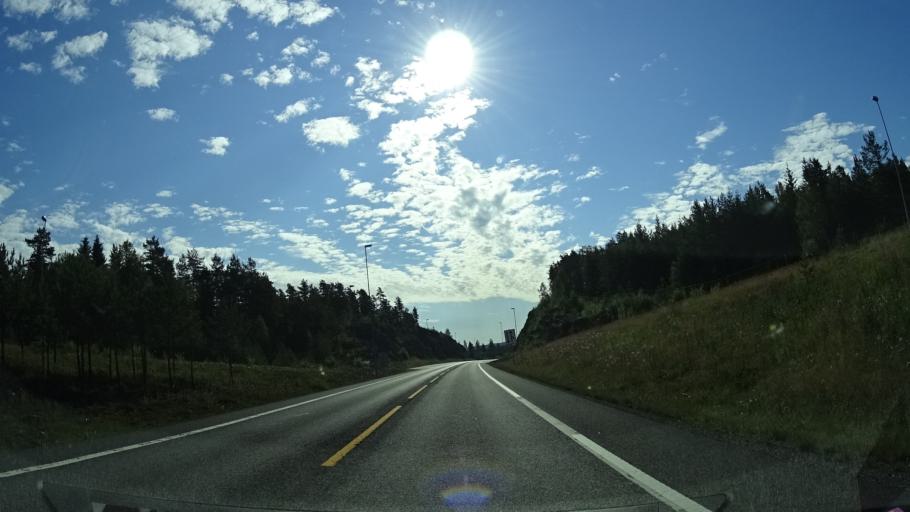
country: NO
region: Ostfold
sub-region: Marker
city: Orje
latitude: 59.5398
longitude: 11.5381
